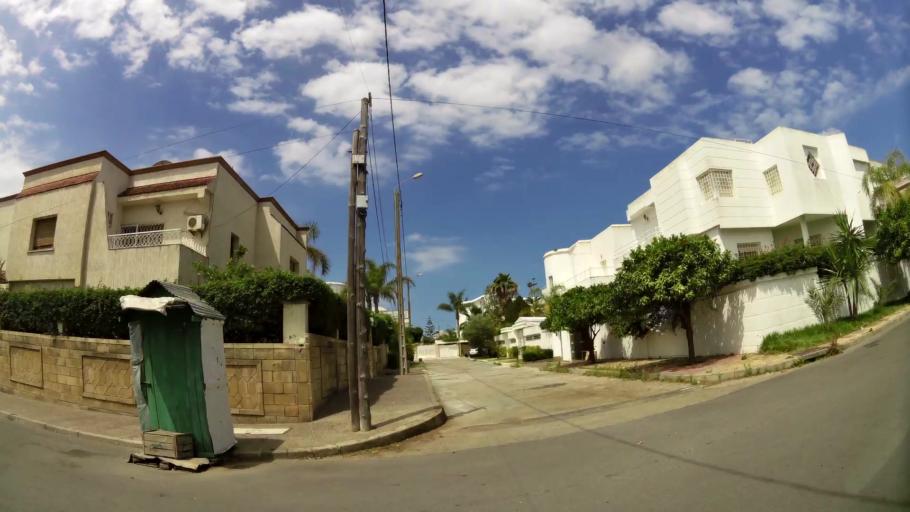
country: MA
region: Gharb-Chrarda-Beni Hssen
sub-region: Kenitra Province
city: Kenitra
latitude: 34.2514
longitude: -6.5978
